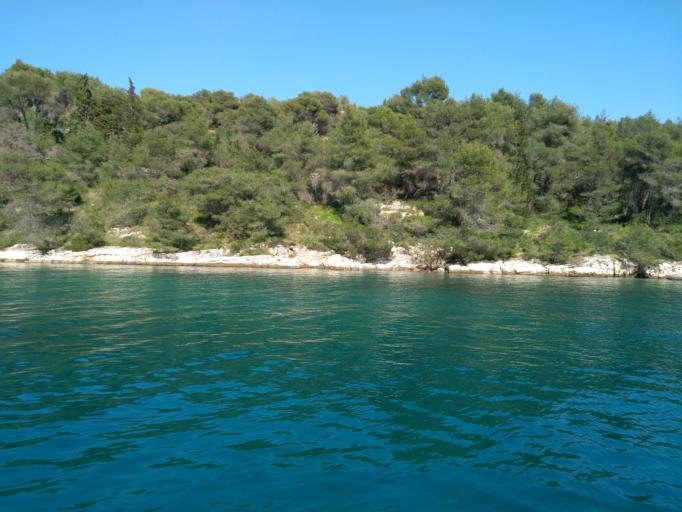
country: HR
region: Splitsko-Dalmatinska
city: Marina
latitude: 43.3751
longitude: 16.4421
